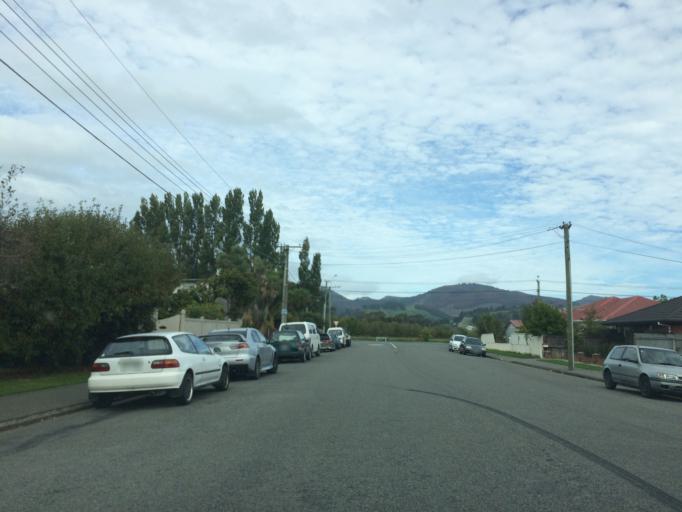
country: NZ
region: Canterbury
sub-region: Christchurch City
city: Christchurch
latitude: -43.5665
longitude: 172.5985
